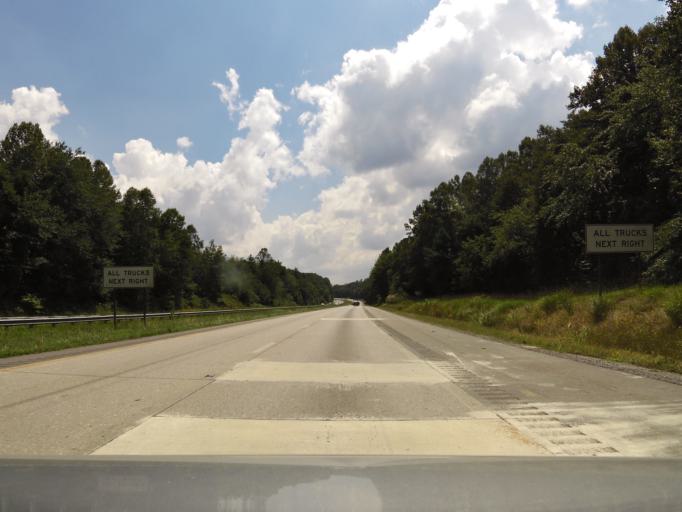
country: US
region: North Carolina
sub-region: Henderson County
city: Mountain Home
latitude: 35.3888
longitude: -82.4898
